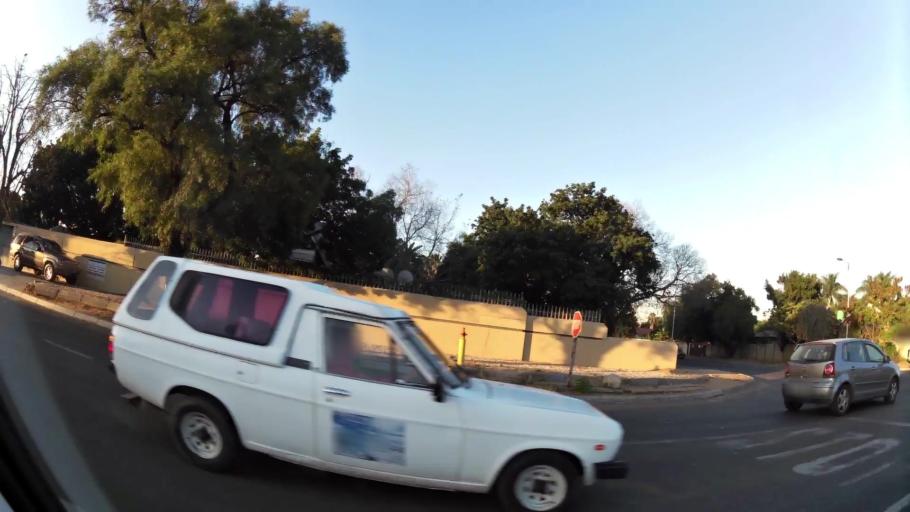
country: ZA
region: North-West
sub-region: Bojanala Platinum District Municipality
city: Rustenburg
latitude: -25.6808
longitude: 27.2208
